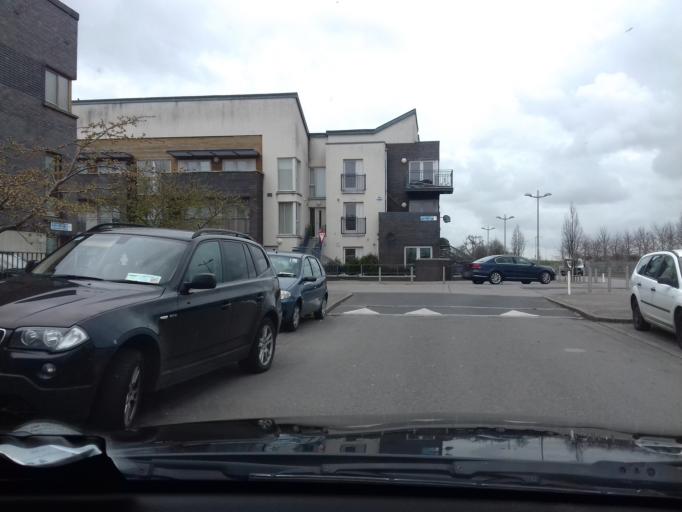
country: IE
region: Leinster
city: Ballymun
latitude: 53.4002
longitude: -6.2695
